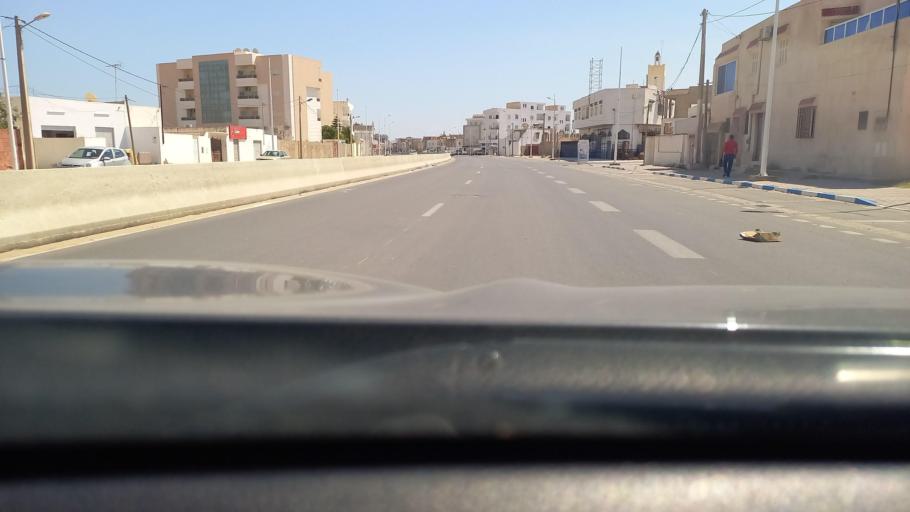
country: TN
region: Safaqis
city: Sfax
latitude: 34.7417
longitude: 10.7240
